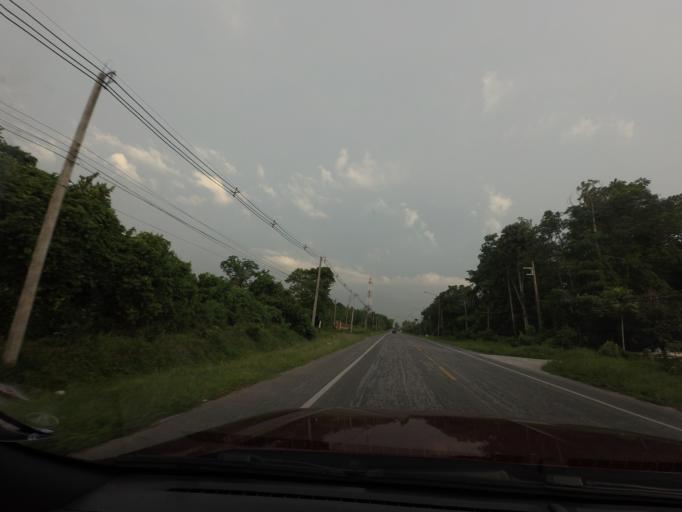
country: TH
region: Pattani
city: Mae Lan
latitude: 6.5910
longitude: 101.1959
